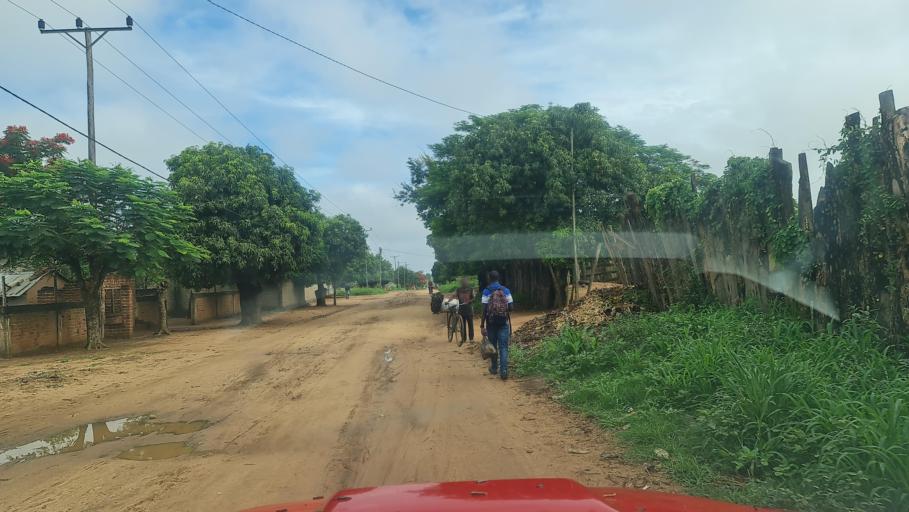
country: MW
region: Southern Region
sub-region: Nsanje District
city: Nsanje
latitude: -17.3197
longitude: 35.5920
